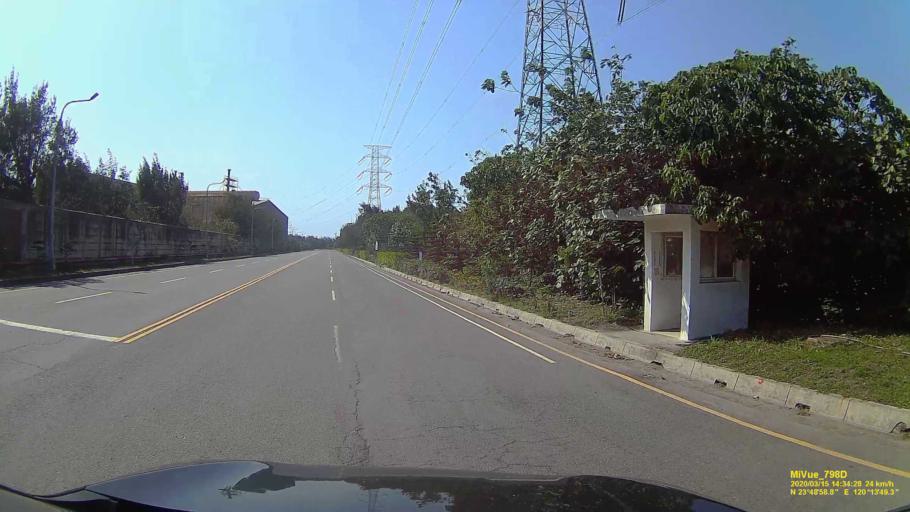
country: TW
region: Taiwan
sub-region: Yunlin
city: Douliu
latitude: 23.8164
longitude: 120.2302
